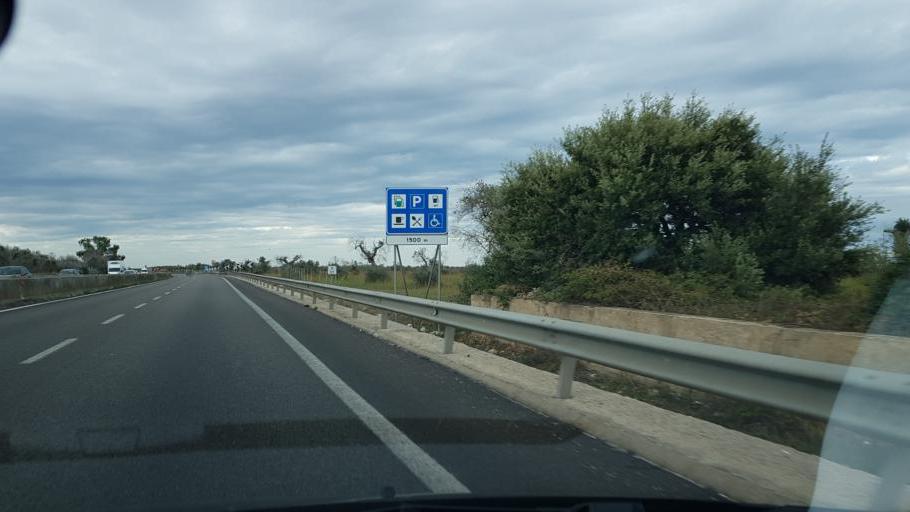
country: IT
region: Apulia
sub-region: Provincia di Lecce
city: Surbo
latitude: 40.4075
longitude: 18.1076
